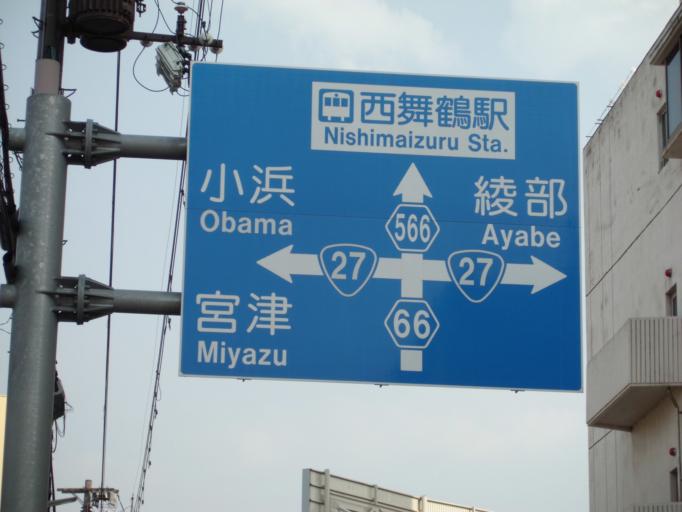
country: JP
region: Kyoto
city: Maizuru
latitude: 35.4428
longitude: 135.3276
